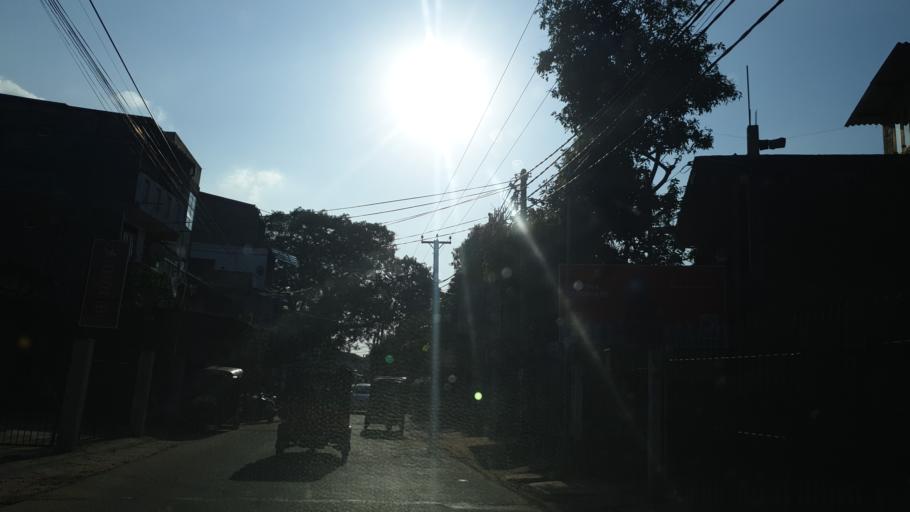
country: LK
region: Western
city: Galkissa
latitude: 6.8505
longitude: 79.8801
